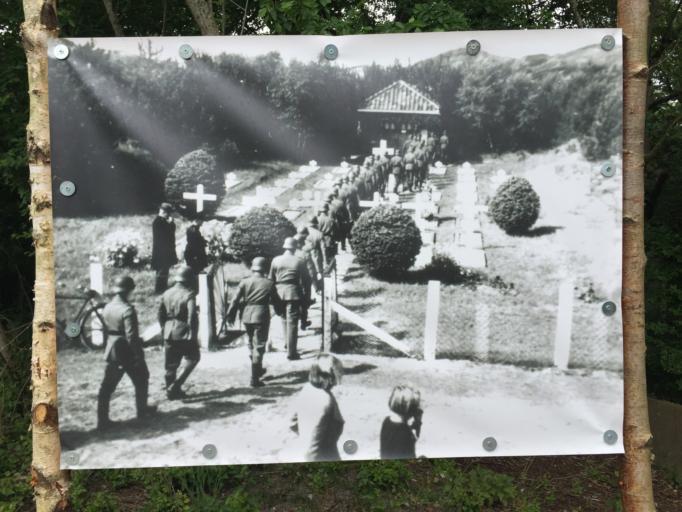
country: NL
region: Friesland
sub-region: Gemeente Schiermonnikoog
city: Schiermonnikoog
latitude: 53.4855
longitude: 6.1857
